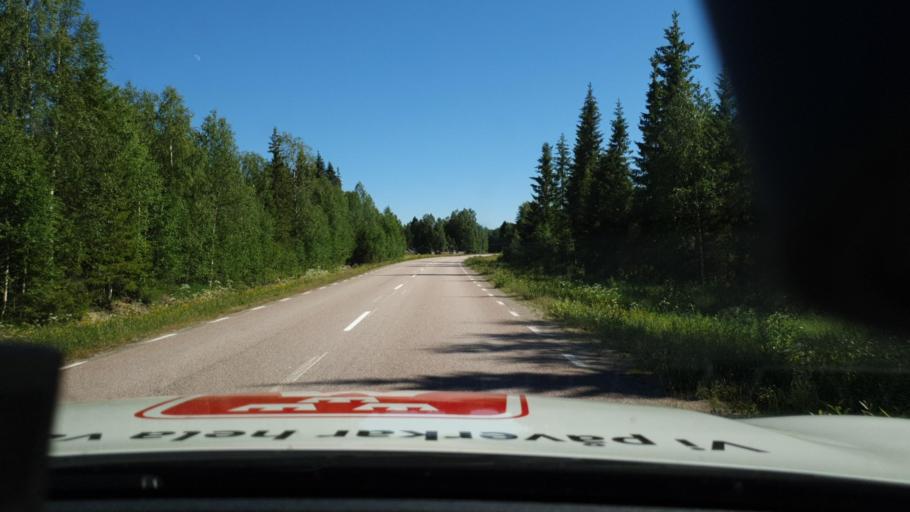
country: SE
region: Norrbotten
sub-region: Lulea Kommun
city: Ranea
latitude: 65.9542
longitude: 22.3937
